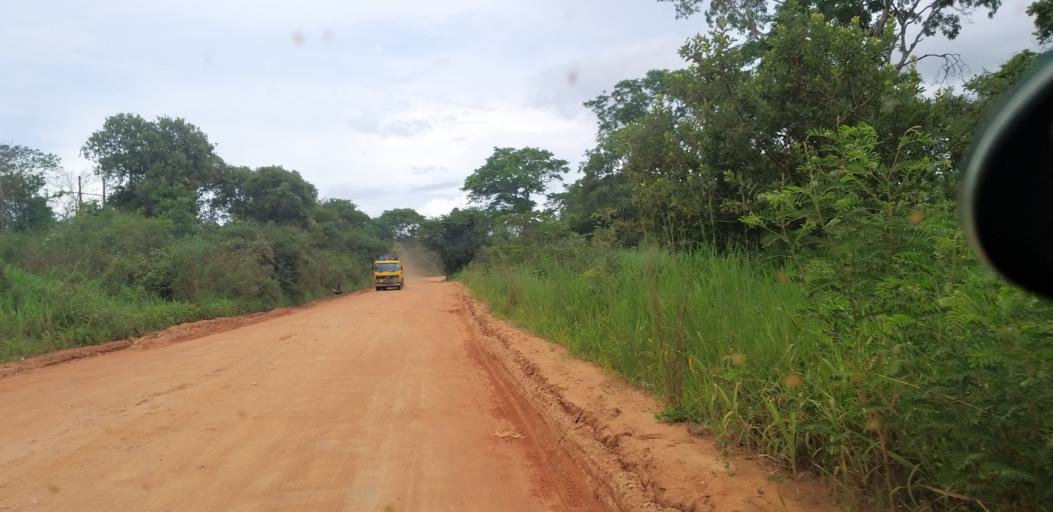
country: ZM
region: Lusaka
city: Lusaka
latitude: -15.2004
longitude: 28.4396
